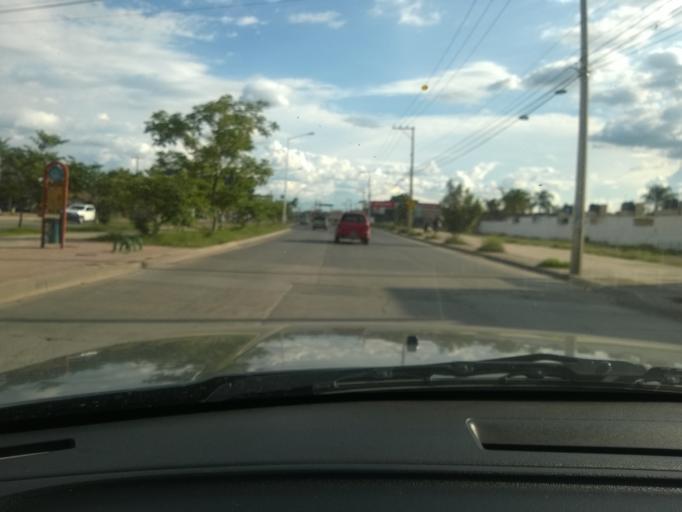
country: MX
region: Guanajuato
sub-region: Leon
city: San Jose de Duran (Los Troncoso)
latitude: 21.0777
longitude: -101.6346
